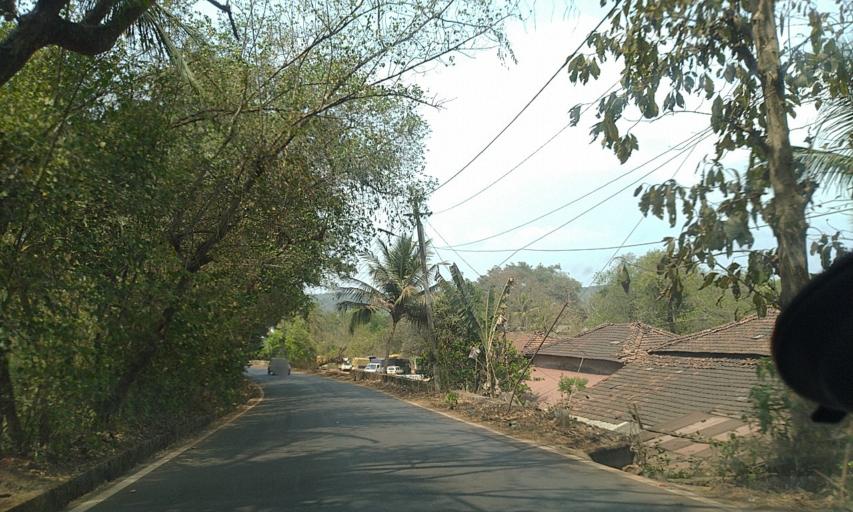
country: IN
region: Goa
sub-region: North Goa
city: Pernem
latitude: 15.7126
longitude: 73.7983
